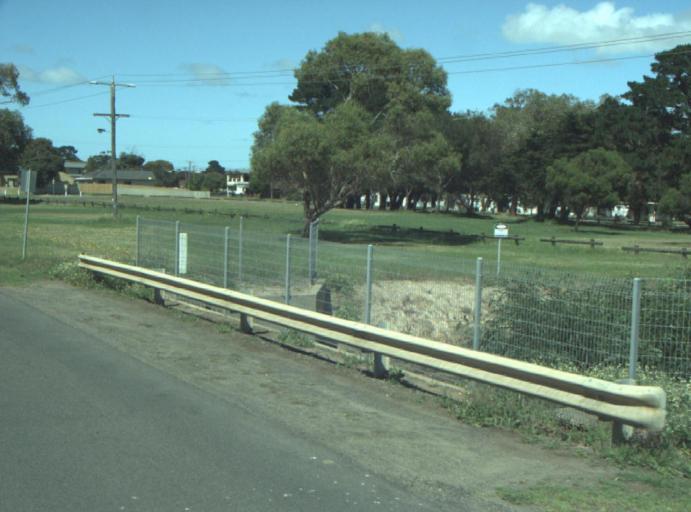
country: AU
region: Victoria
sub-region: Queenscliffe
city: Queenscliff
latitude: -38.1780
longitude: 144.7158
